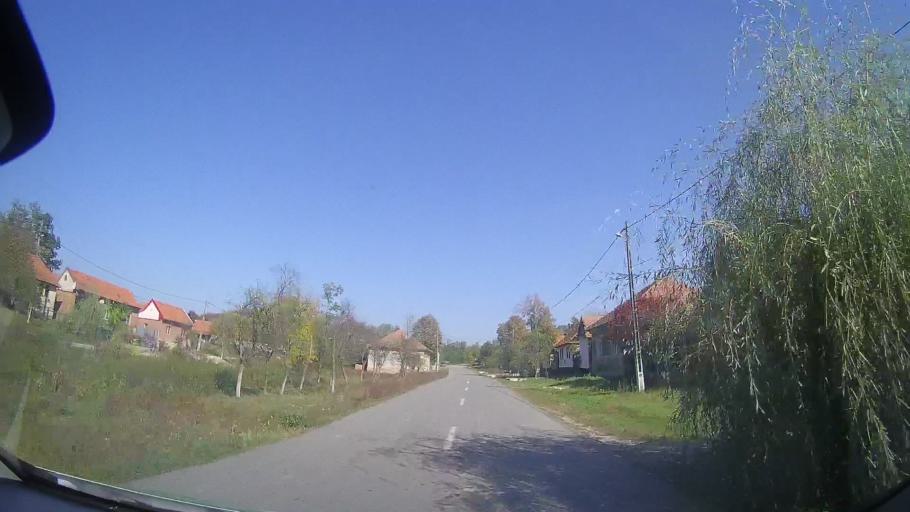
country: RO
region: Timis
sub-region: Comuna Bara
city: Bara
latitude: 45.8962
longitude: 21.8815
